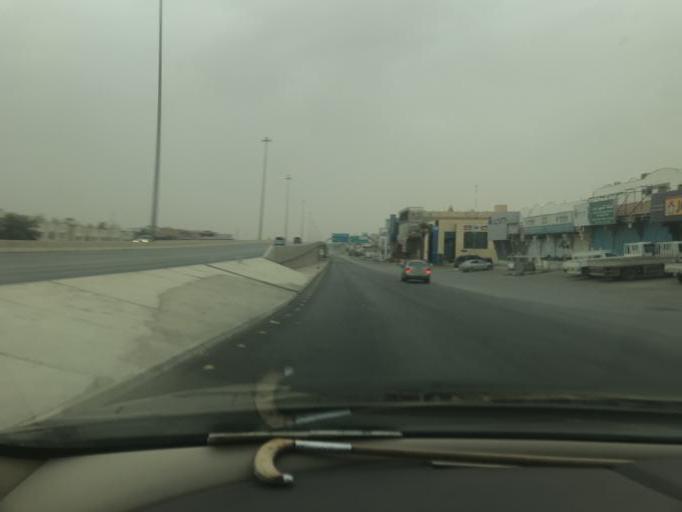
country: SA
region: Ar Riyad
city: Riyadh
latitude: 24.7874
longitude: 46.7034
